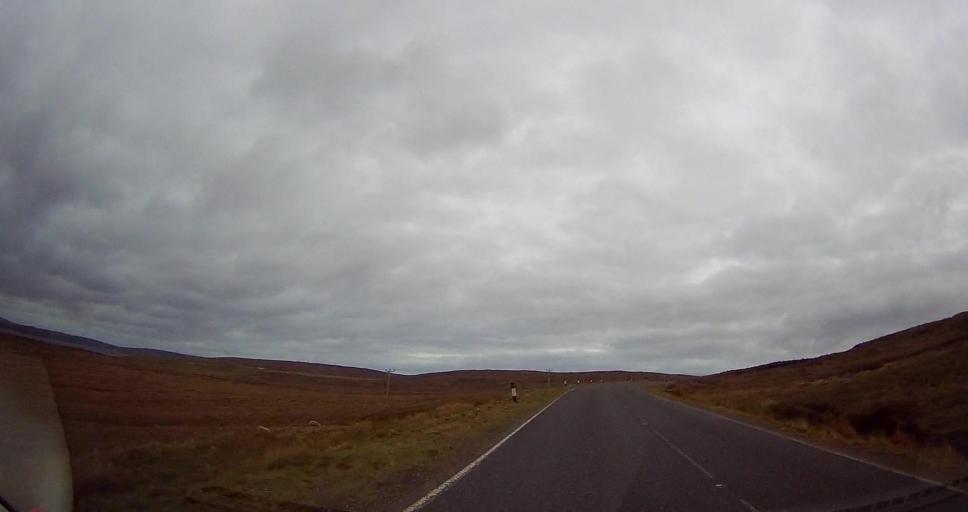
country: GB
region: Scotland
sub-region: Shetland Islands
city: Shetland
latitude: 60.6389
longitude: -1.0675
